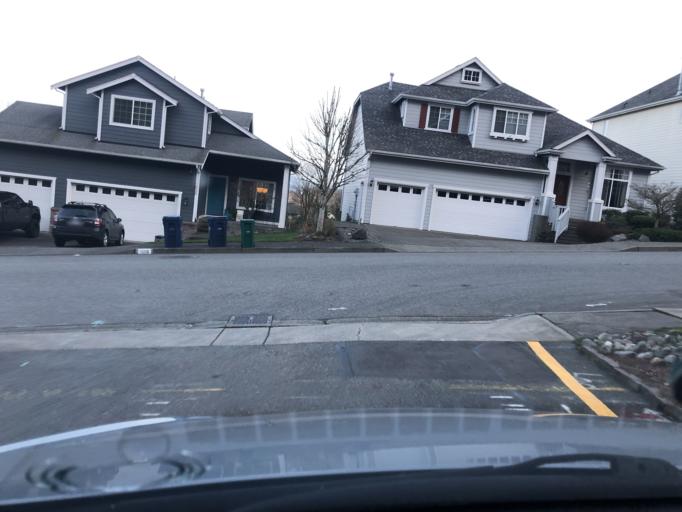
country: US
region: Washington
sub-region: King County
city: Auburn
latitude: 47.3176
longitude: -122.2530
